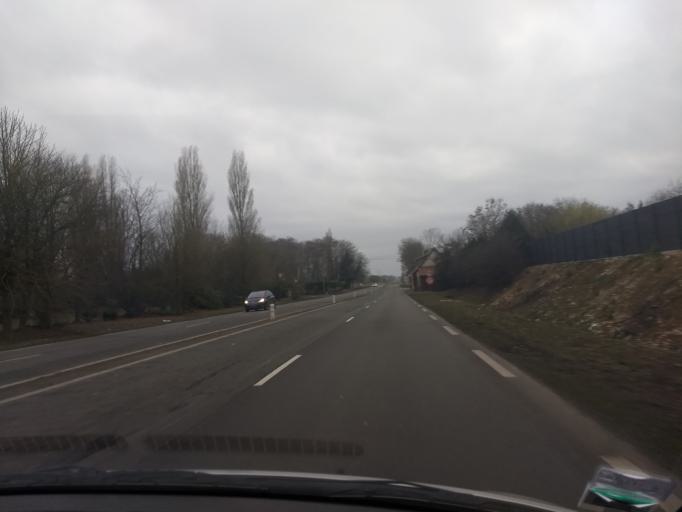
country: FR
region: Nord-Pas-de-Calais
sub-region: Departement du Pas-de-Calais
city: Feuchy
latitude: 50.2708
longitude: 2.8509
